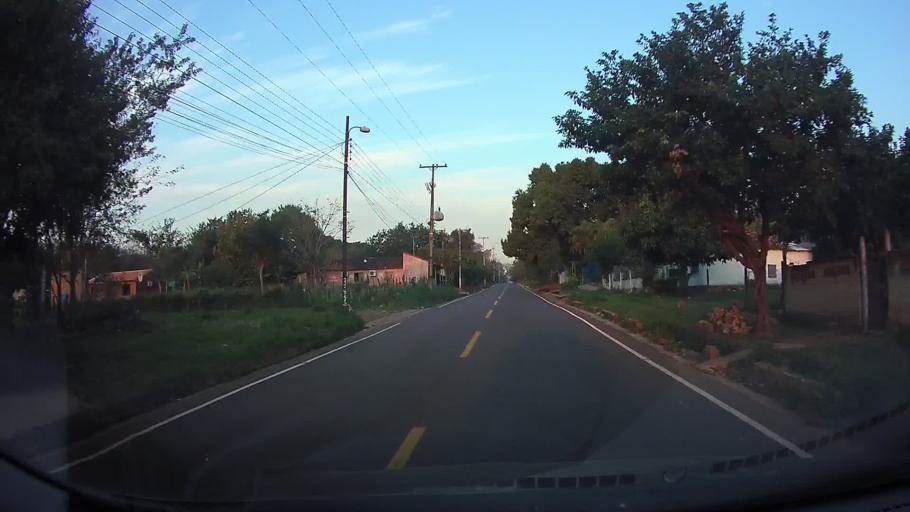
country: PY
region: Central
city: Limpio
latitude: -25.2361
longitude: -57.4894
